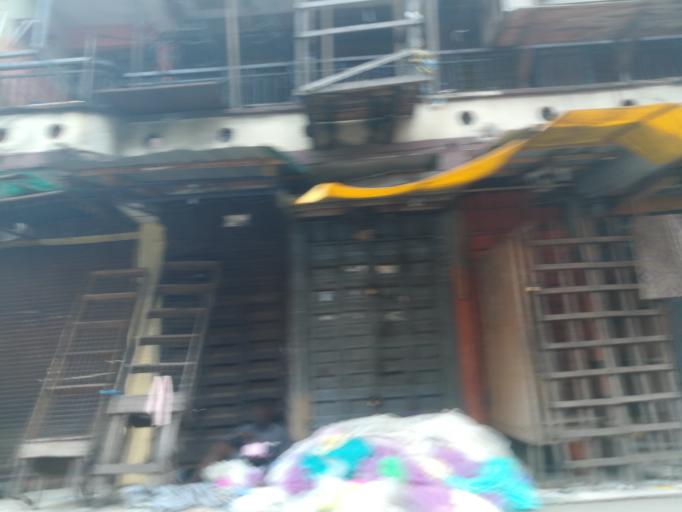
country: NG
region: Lagos
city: Lagos
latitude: 6.4590
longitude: 3.3879
